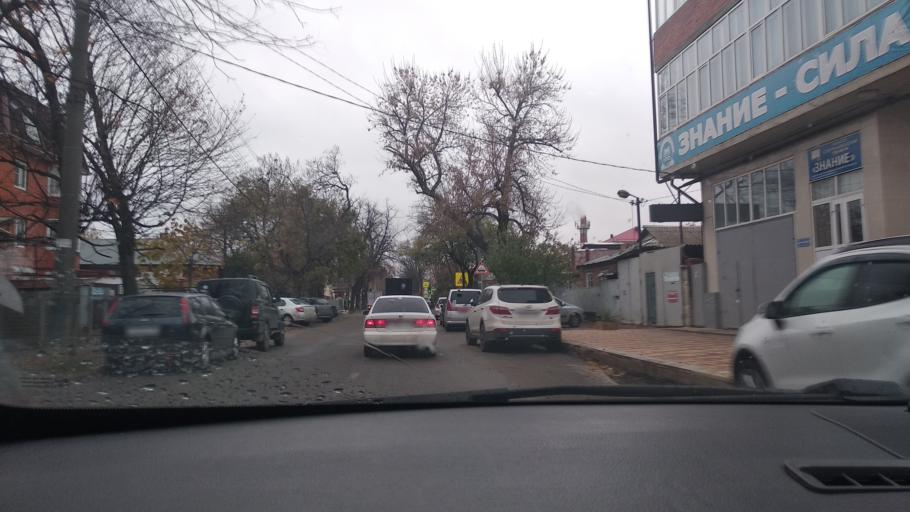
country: RU
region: Krasnodarskiy
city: Krasnodar
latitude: 45.0284
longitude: 38.9829
